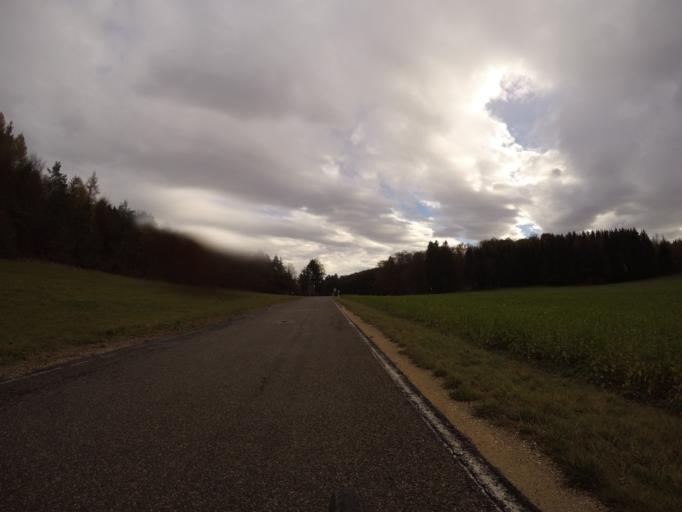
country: DE
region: Baden-Wuerttemberg
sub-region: Tuebingen Region
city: Sankt Johann
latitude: 48.4110
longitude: 9.2950
